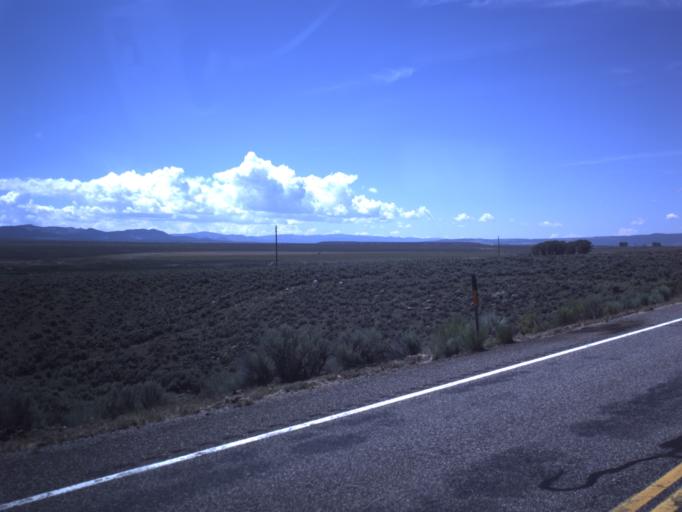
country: US
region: Utah
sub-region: Garfield County
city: Panguitch
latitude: 37.9915
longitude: -112.3921
